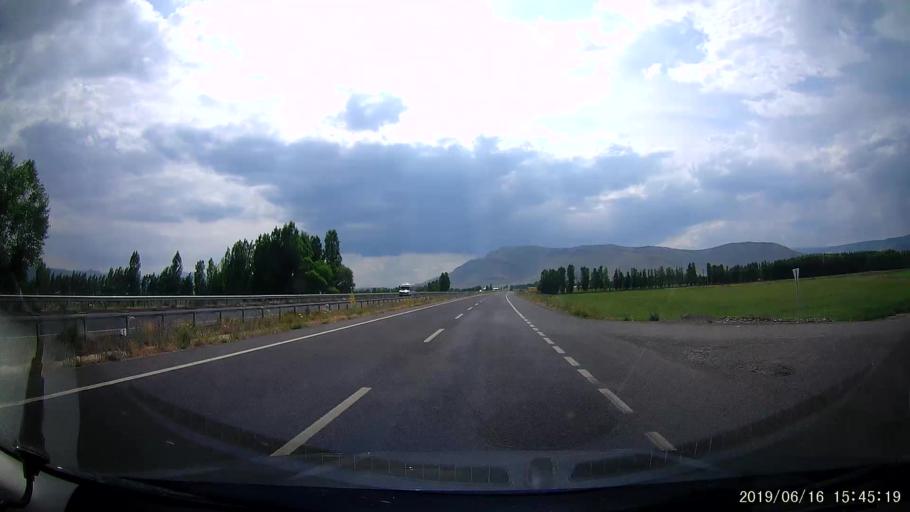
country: TR
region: Erzurum
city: Pasinler
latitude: 39.9882
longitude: 41.7689
